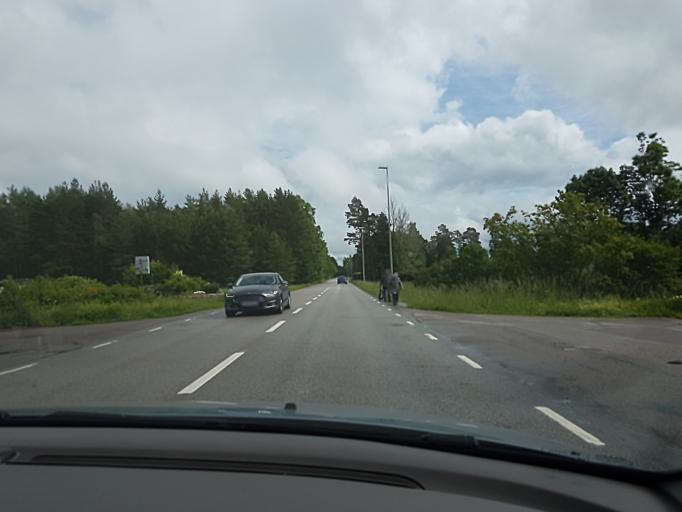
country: SE
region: Uppsala
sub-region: Osthammars Kommun
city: OEsthammar
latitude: 60.2822
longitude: 18.2946
